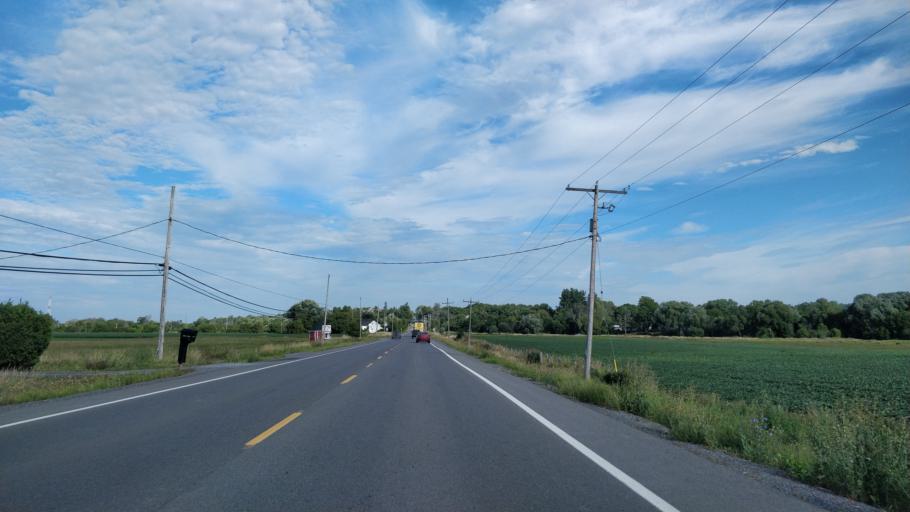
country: CA
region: Ontario
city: Bells Corners
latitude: 45.3388
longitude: -76.0287
